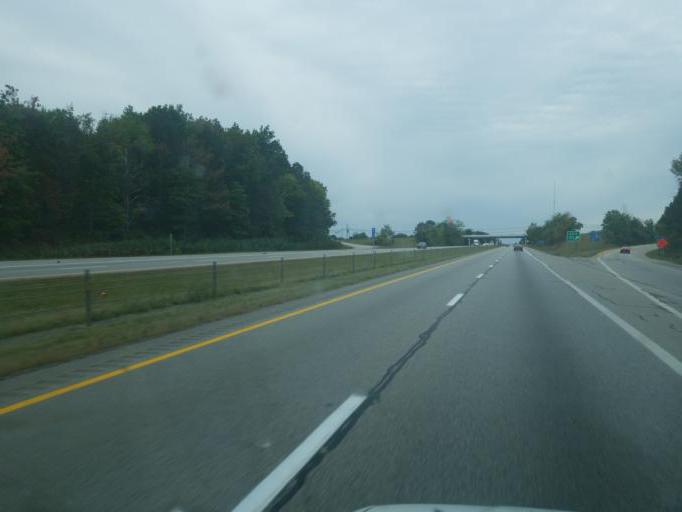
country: US
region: Ohio
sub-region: Portage County
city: Brimfield
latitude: 41.1078
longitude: -81.3426
